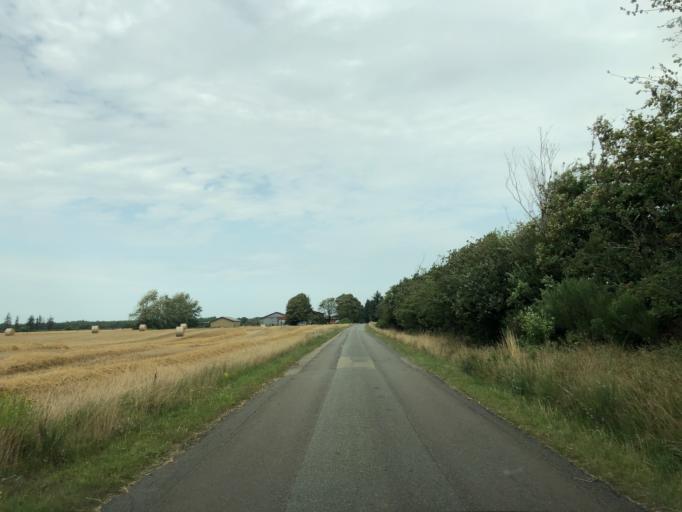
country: DK
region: Central Jutland
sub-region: Holstebro Kommune
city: Ulfborg
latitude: 56.2114
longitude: 8.3177
